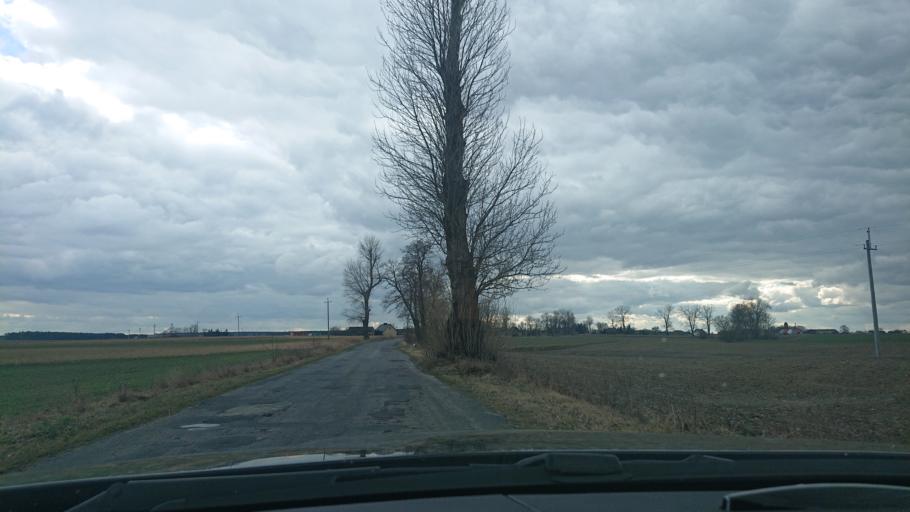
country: PL
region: Greater Poland Voivodeship
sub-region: Powiat gnieznienski
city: Gniezno
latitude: 52.5801
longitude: 17.6858
